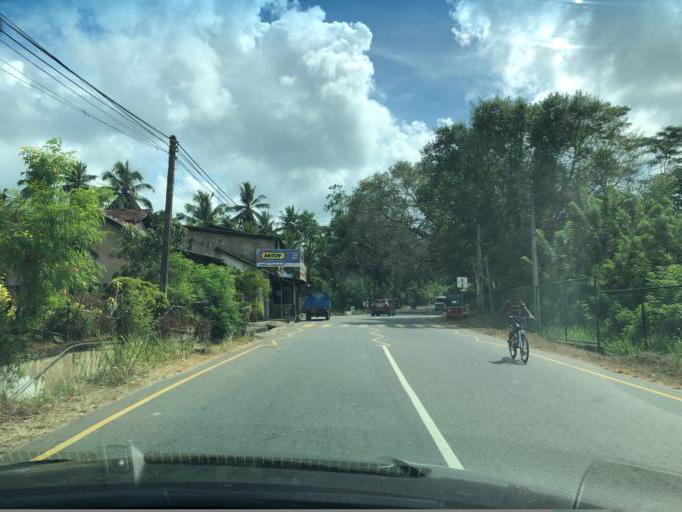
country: LK
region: Western
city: Horana South
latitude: 6.6242
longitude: 80.0757
